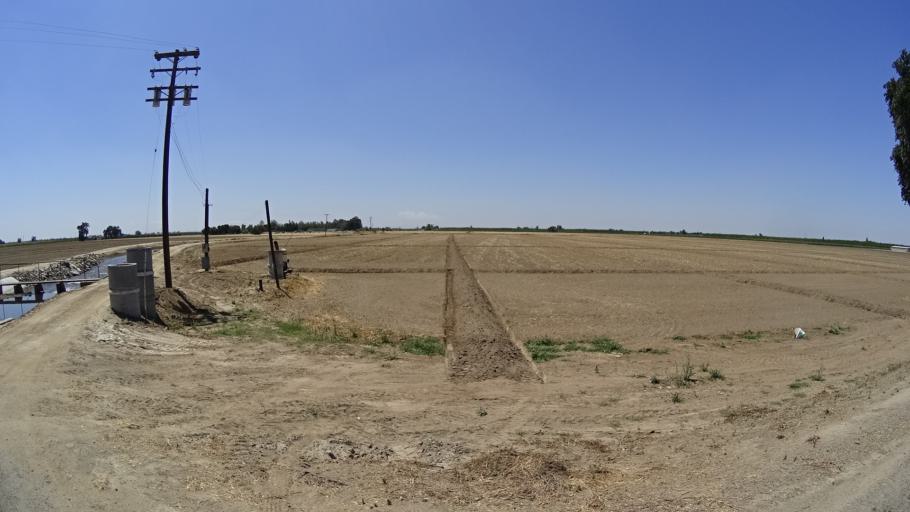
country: US
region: California
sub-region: Kings County
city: Lucerne
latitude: 36.3905
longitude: -119.6191
